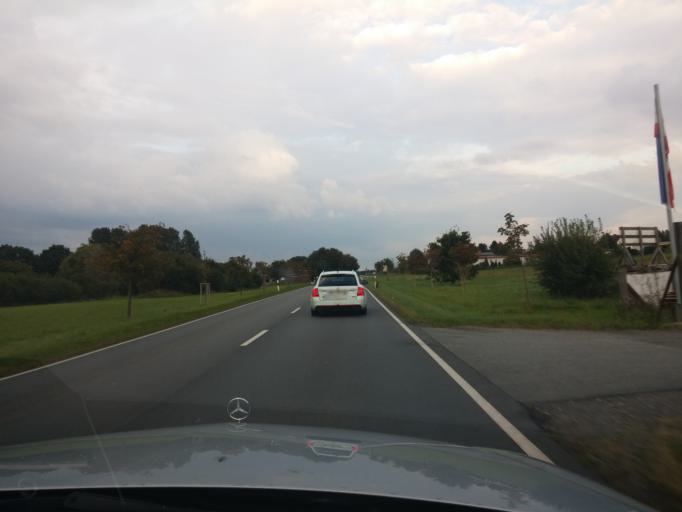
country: DE
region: Mecklenburg-Vorpommern
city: Selmsdorf
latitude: 53.8841
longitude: 10.8547
